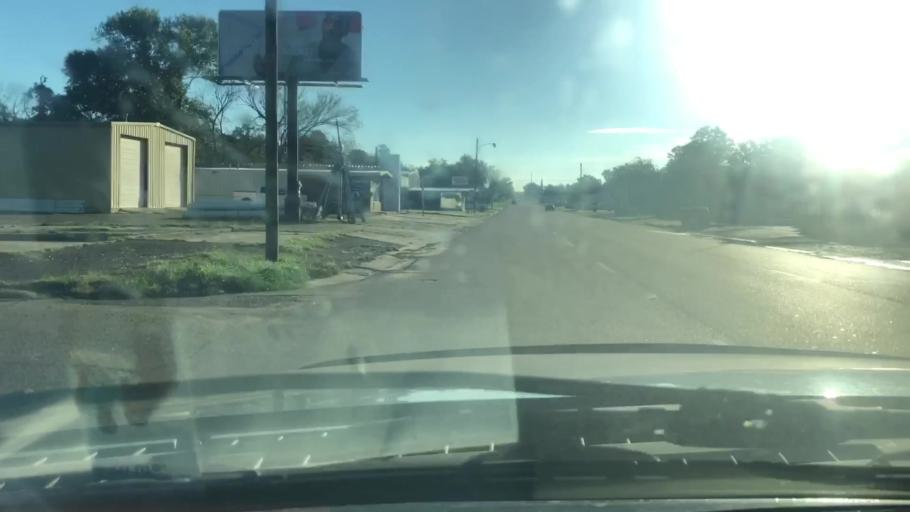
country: US
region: Texas
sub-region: Bowie County
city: Texarkana
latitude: 33.4232
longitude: -94.0681
